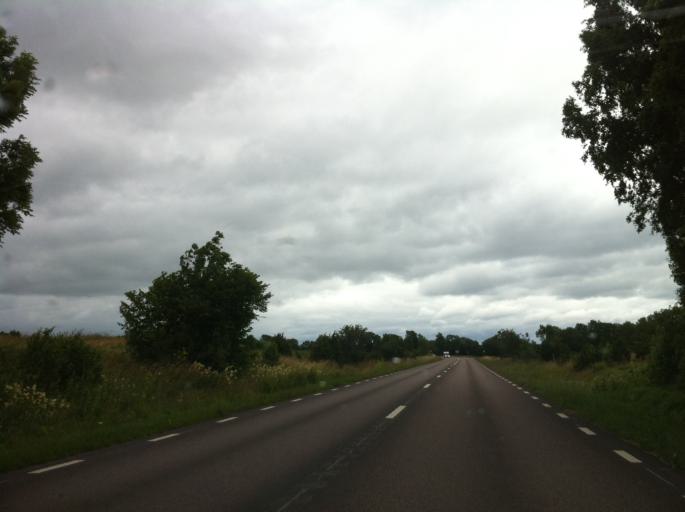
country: SE
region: Kalmar
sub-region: Borgholms Kommun
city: Borgholm
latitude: 57.1410
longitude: 16.9978
